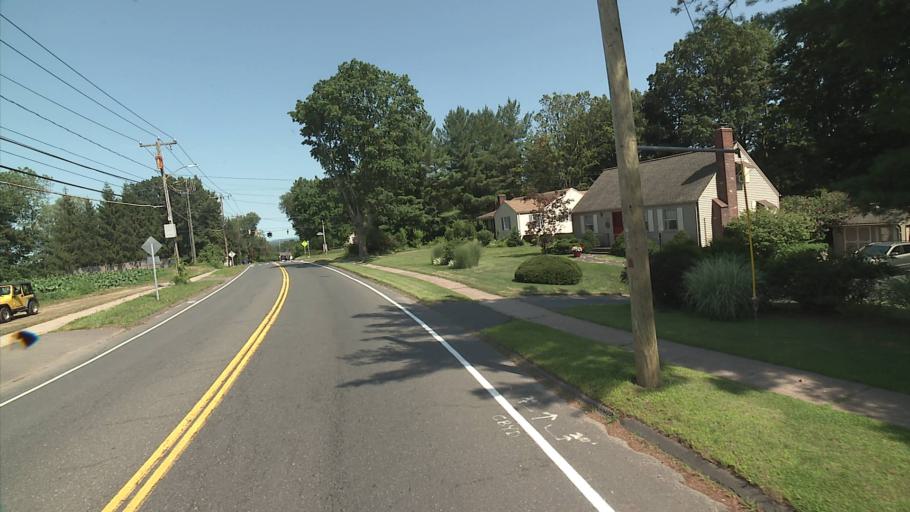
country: US
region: Connecticut
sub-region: Hartford County
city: Windsor
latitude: 41.8517
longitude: -72.6586
